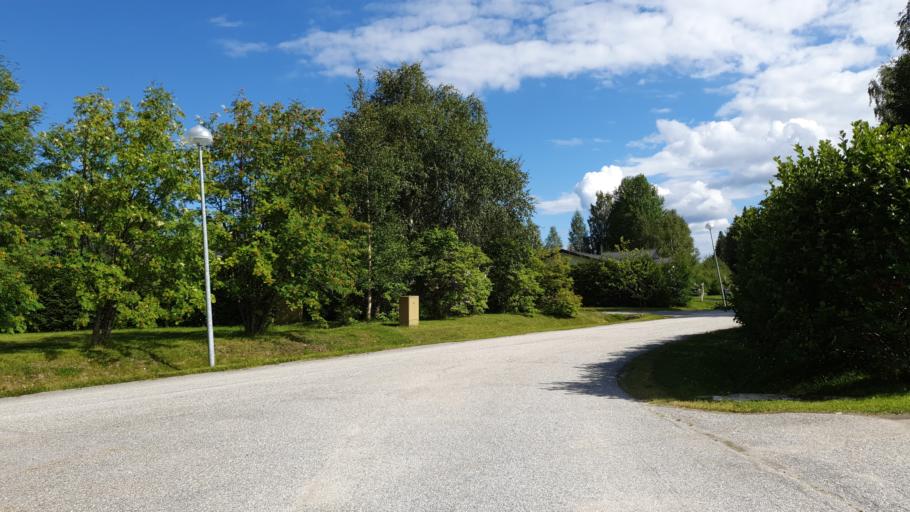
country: FI
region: Kainuu
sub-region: Kehys-Kainuu
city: Kuhmo
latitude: 64.1212
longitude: 29.4951
